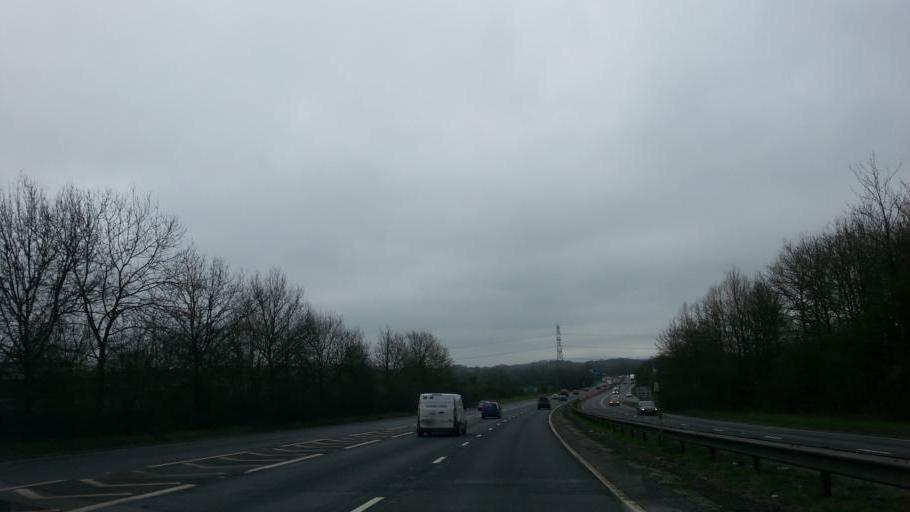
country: GB
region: England
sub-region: Devon
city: Uffculme
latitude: 50.9229
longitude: -3.3654
